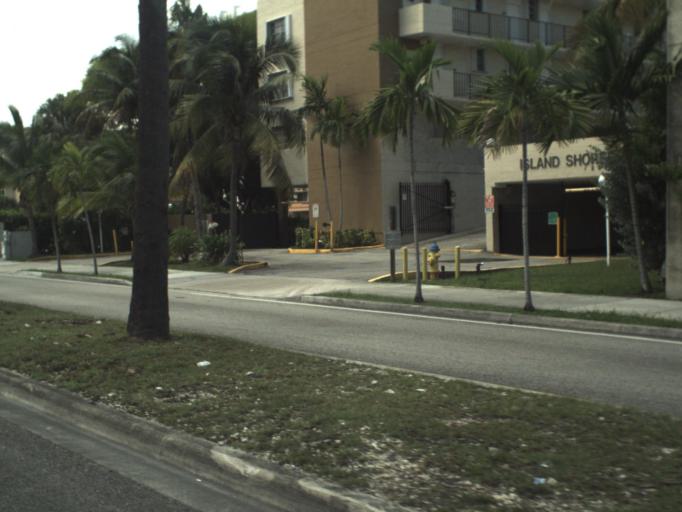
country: US
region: Florida
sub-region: Miami-Dade County
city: North Miami Beach
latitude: 25.9264
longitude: -80.1418
